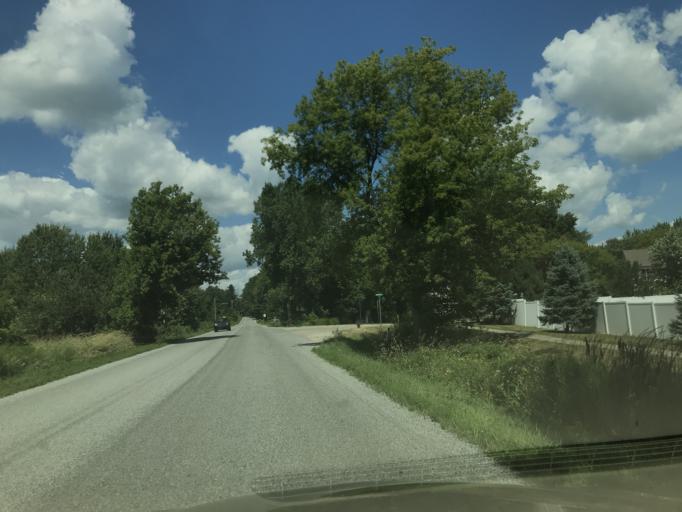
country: US
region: Michigan
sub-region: Ingham County
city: Holt
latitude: 42.6268
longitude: -84.5627
